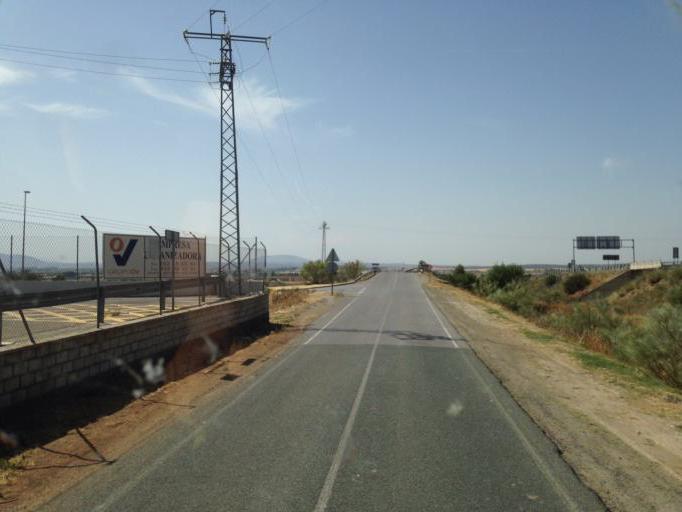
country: ES
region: Andalusia
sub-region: Provincia de Malaga
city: Antequera
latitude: 37.0446
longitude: -4.5108
